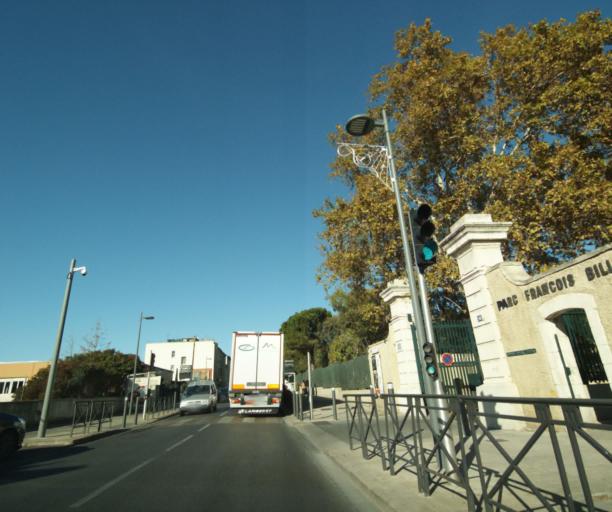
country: FR
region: Provence-Alpes-Cote d'Azur
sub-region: Departement des Bouches-du-Rhone
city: Marseille 14
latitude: 43.3323
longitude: 5.3645
